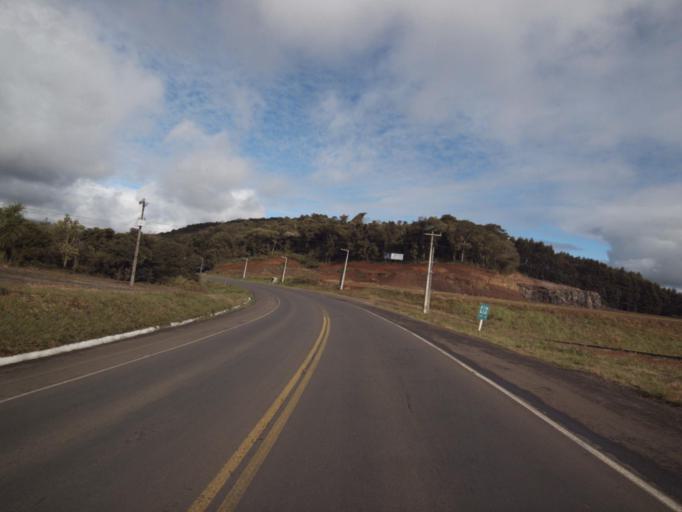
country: BR
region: Santa Catarina
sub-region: Concordia
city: Concordia
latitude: -27.2030
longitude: -51.9480
